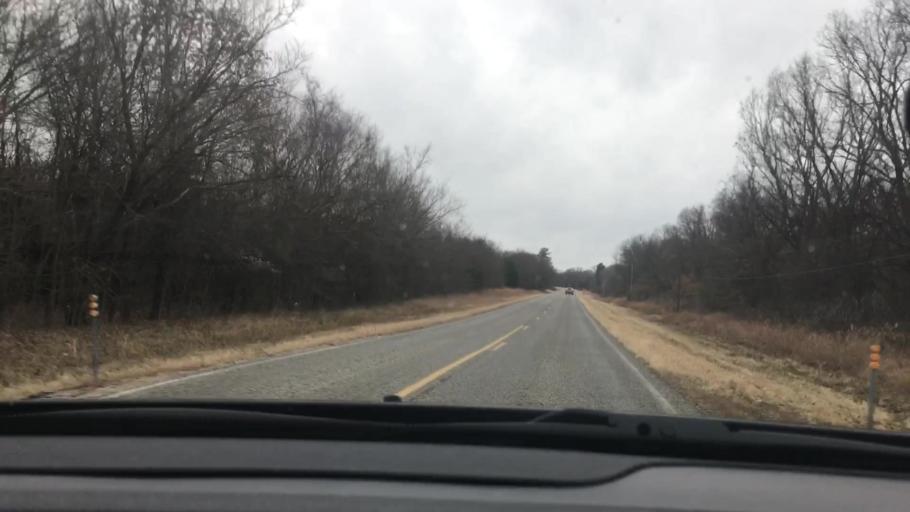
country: US
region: Oklahoma
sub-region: Johnston County
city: Tishomingo
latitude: 34.2157
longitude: -96.6361
